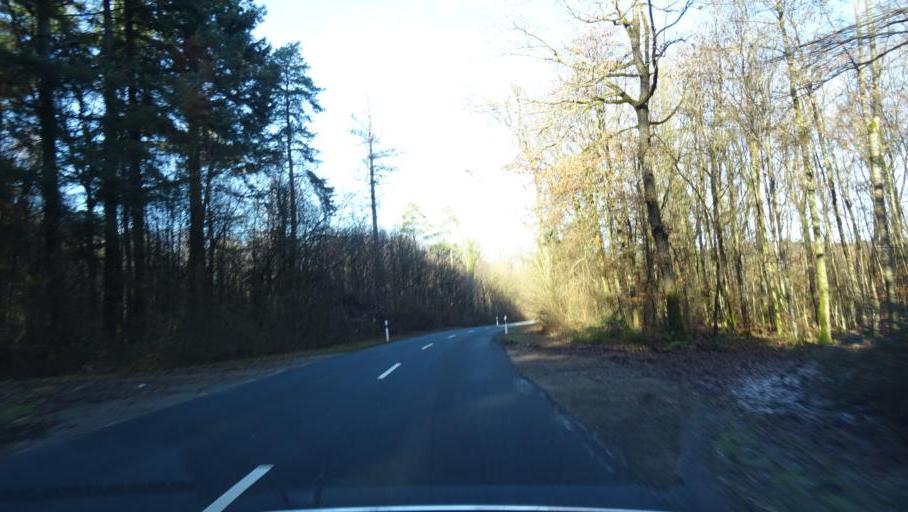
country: DE
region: Baden-Wuerttemberg
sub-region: Karlsruhe Region
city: Obrigheim
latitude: 49.3839
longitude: 9.1089
